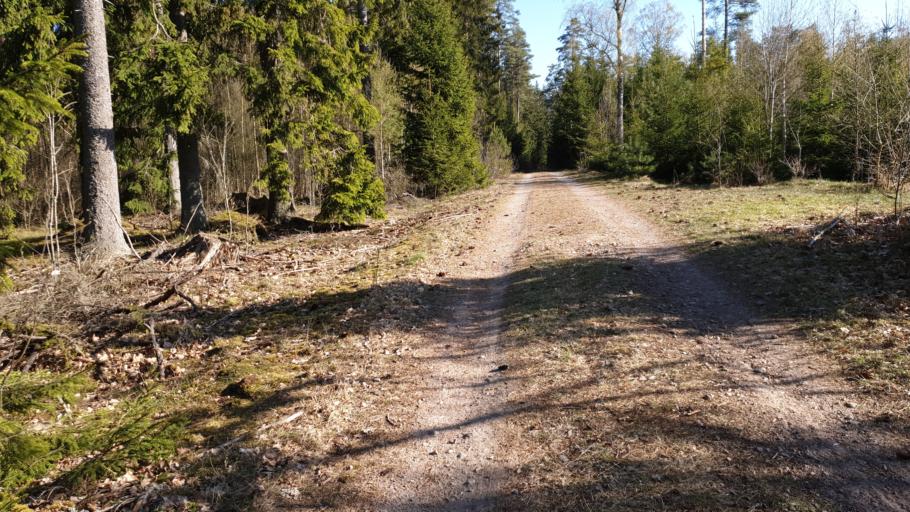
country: SE
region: Kronoberg
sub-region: Ljungby Kommun
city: Ljungby
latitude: 56.8305
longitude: 13.9017
